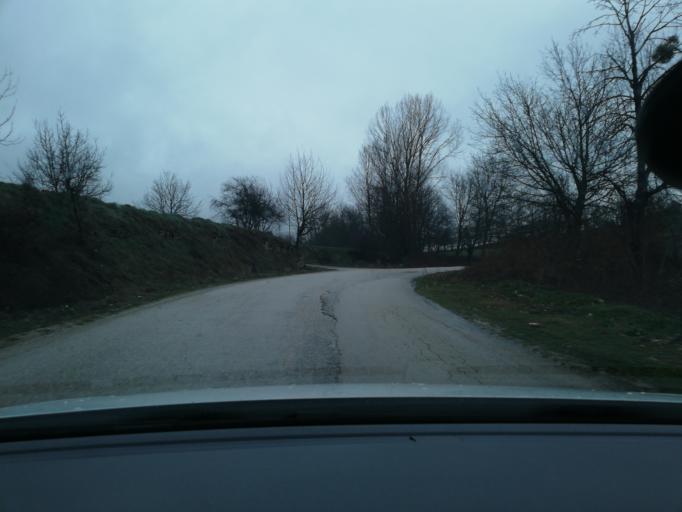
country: TR
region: Bolu
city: Bolu
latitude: 40.7722
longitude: 31.6491
